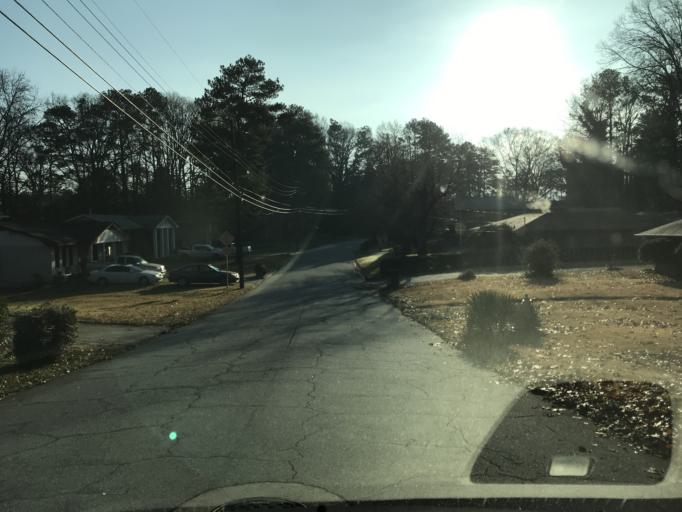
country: US
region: Georgia
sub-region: Fulton County
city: College Park
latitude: 33.6143
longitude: -84.4316
